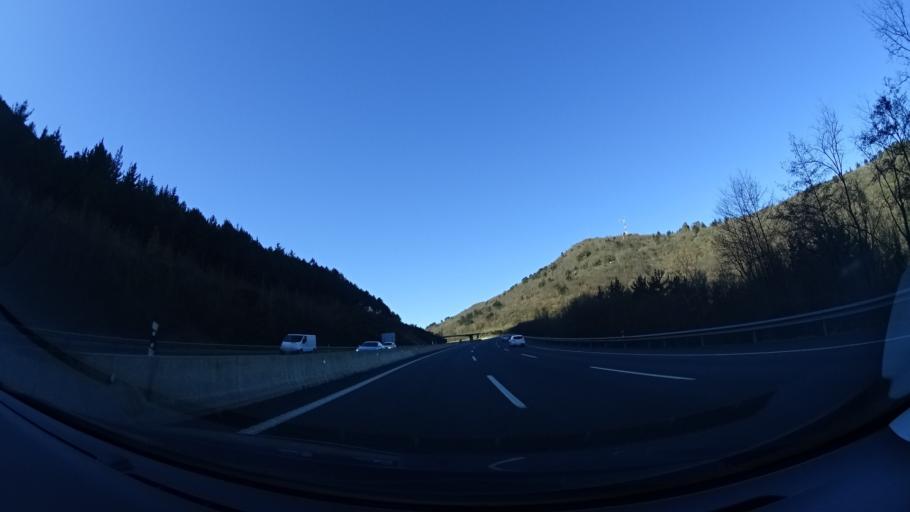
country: ES
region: Basque Country
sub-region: Provincia de Guipuzcoa
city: Usurbil
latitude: 43.2954
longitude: -2.0553
